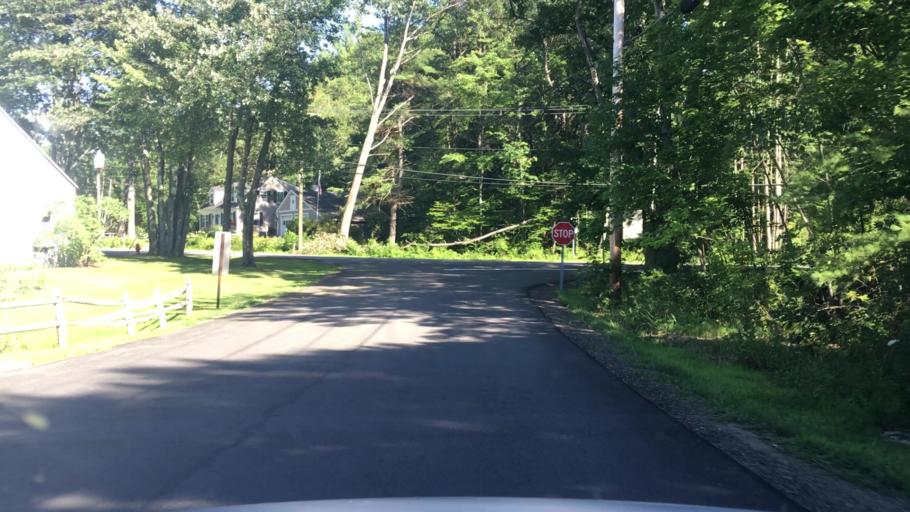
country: US
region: New Hampshire
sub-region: Rockingham County
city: Newmarket
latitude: 43.0378
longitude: -70.9505
